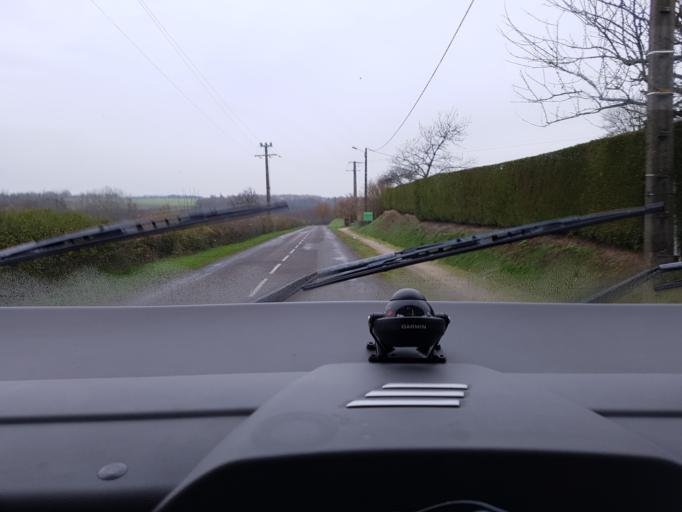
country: FR
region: Haute-Normandie
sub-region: Departement de l'Eure
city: Rugles
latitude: 48.9106
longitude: 0.7478
